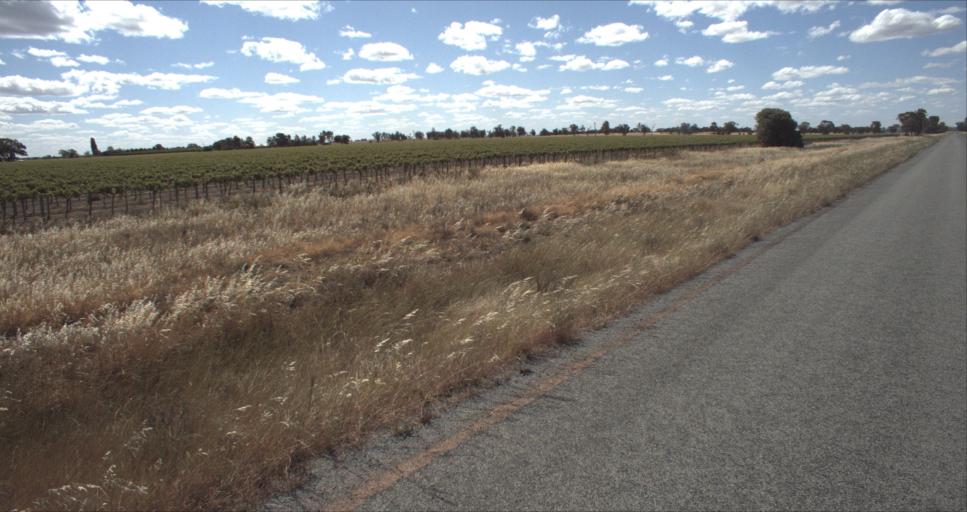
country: AU
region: New South Wales
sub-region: Leeton
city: Leeton
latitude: -34.4970
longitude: 146.2462
